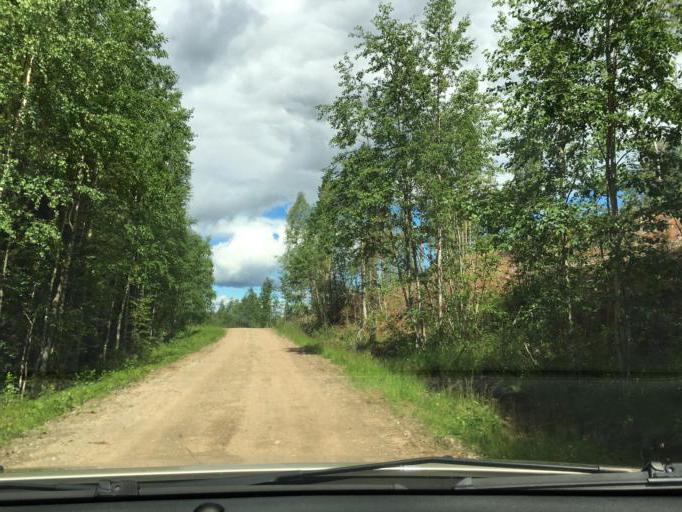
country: SE
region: Norrbotten
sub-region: Overkalix Kommun
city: OEverkalix
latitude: 66.1604
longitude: 22.8555
